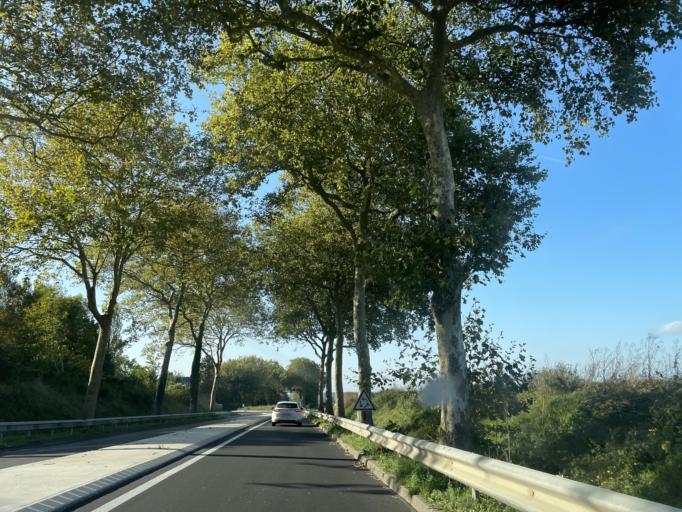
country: FR
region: Ile-de-France
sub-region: Departement de Seine-et-Marne
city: La Chapelle-sur-Crecy
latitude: 48.8474
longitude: 2.9422
